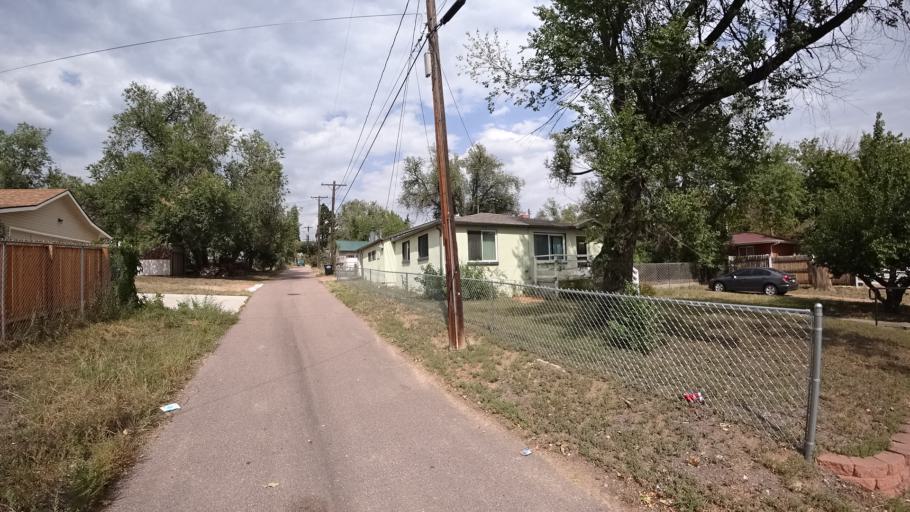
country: US
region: Colorado
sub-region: El Paso County
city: Colorado Springs
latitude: 38.8437
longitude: -104.7894
